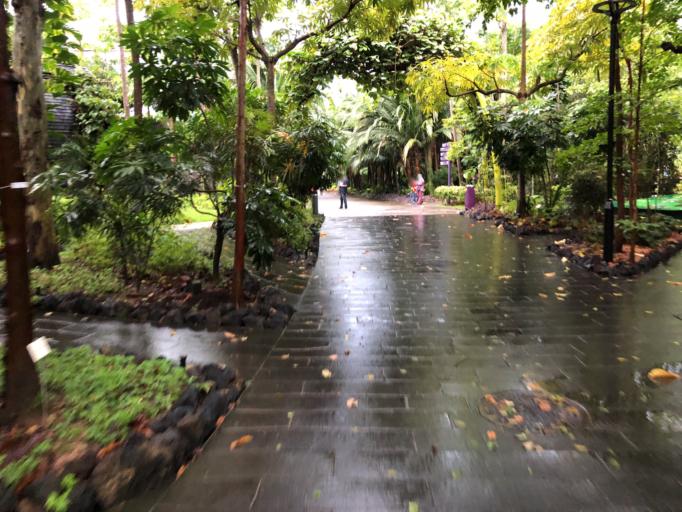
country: SG
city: Singapore
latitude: 1.2828
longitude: 103.8650
